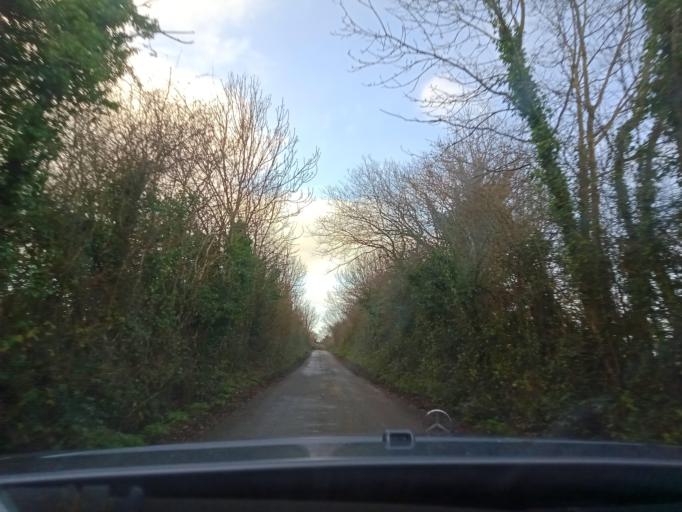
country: IE
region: Leinster
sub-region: Kilkenny
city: Callan
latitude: 52.4759
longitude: -7.3804
